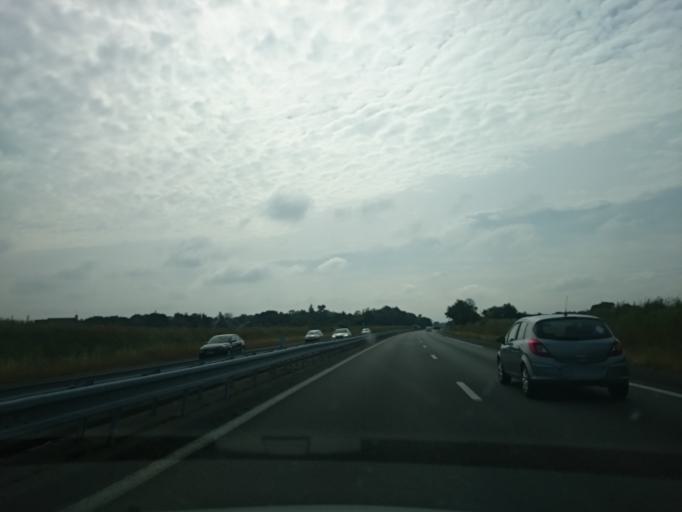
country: FR
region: Brittany
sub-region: Departement du Morbihan
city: Surzur
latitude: 47.5999
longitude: -2.5842
